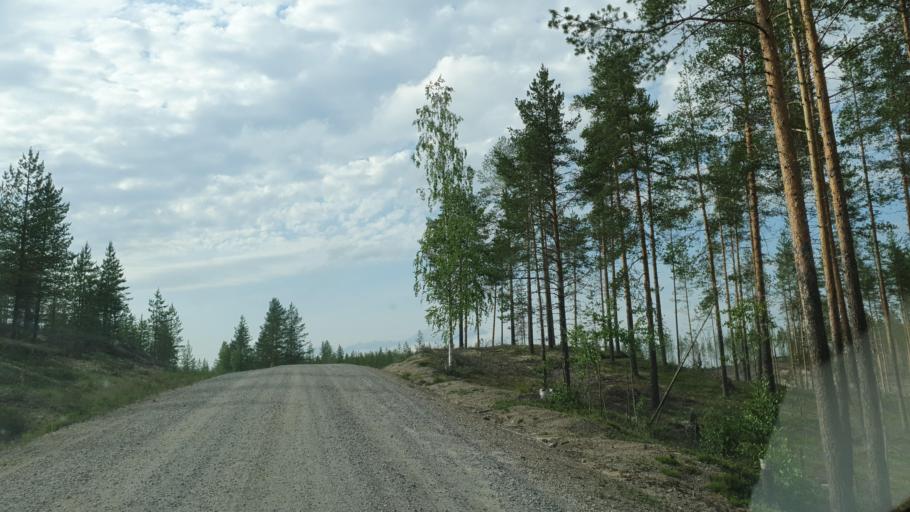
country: FI
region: Kainuu
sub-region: Kehys-Kainuu
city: Kuhmo
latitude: 64.0210
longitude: 29.8951
